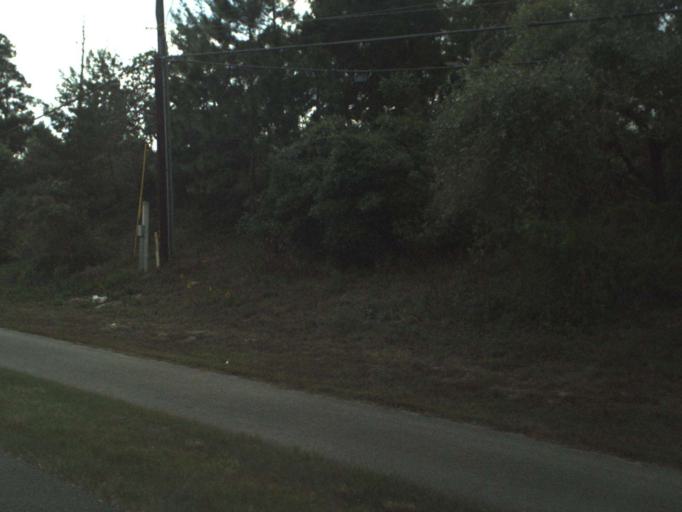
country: US
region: Florida
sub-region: Brevard County
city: Titusville
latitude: 28.6009
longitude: -80.8384
